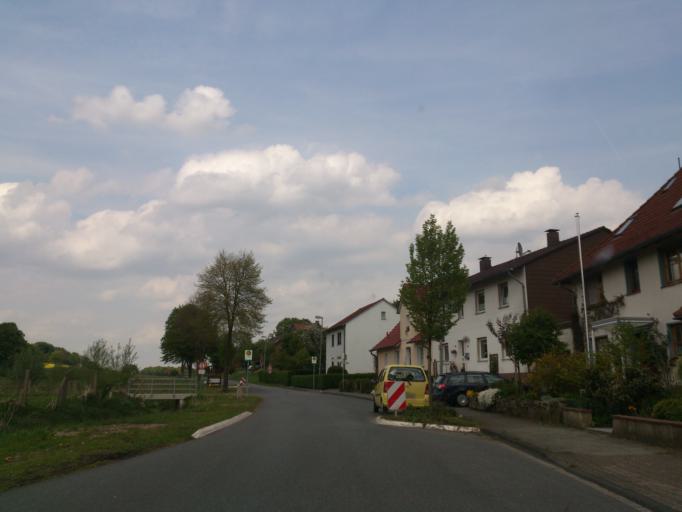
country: DE
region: North Rhine-Westphalia
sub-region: Regierungsbezirk Detmold
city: Altenbeken
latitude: 51.7181
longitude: 8.9346
